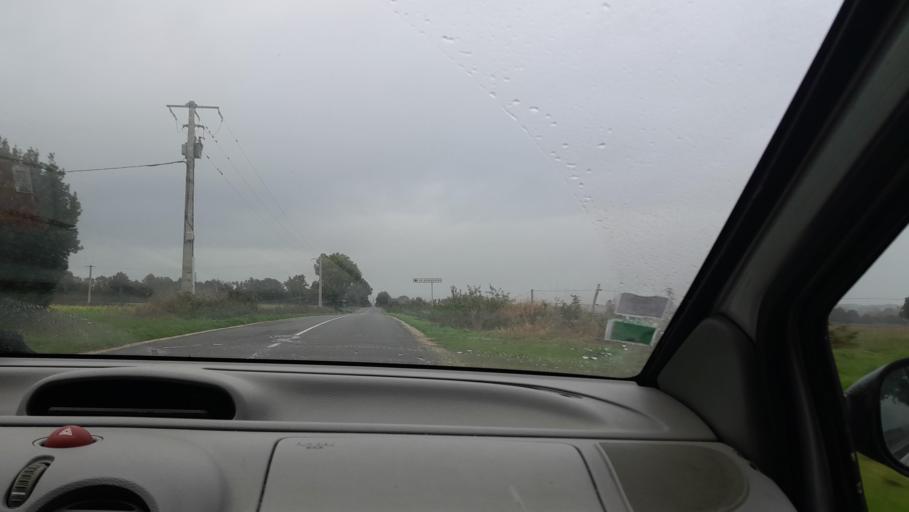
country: FR
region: Pays de la Loire
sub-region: Departement de la Mayenne
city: Congrier
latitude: 47.8240
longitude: -1.1438
